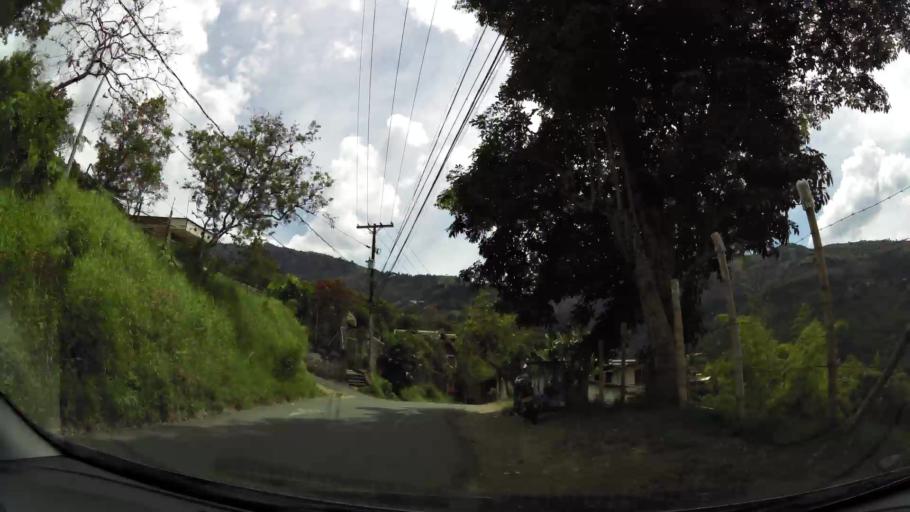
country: CO
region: Antioquia
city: Municipio de Copacabana
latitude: 6.3295
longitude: -75.4996
